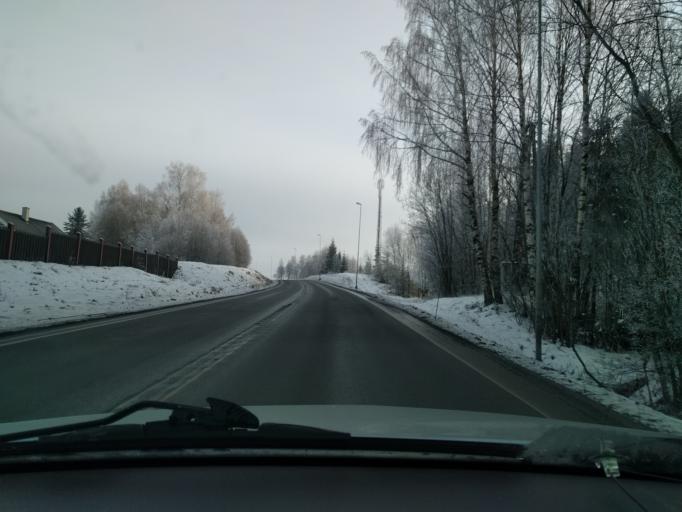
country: NO
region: Hedmark
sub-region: Stange
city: Stange
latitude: 60.8143
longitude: 11.1781
